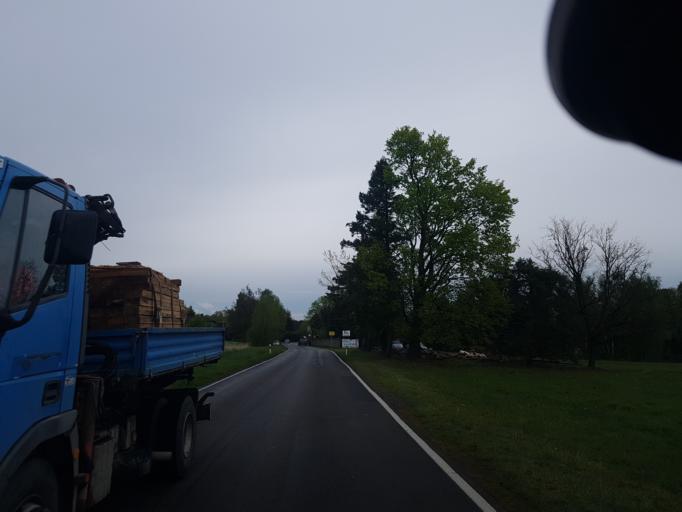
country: DE
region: Brandenburg
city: Spremberg
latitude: 51.6137
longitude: 14.4106
